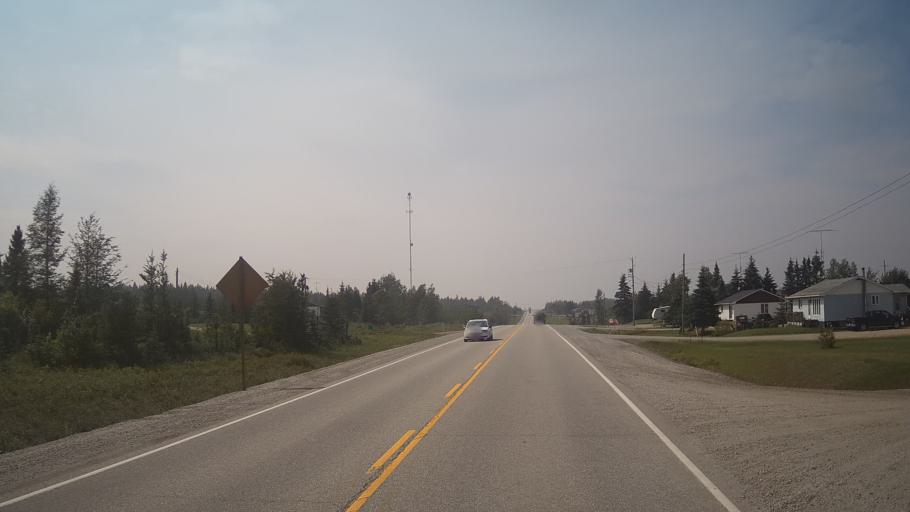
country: CA
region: Ontario
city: Kapuskasing
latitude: 49.3192
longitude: -82.0572
